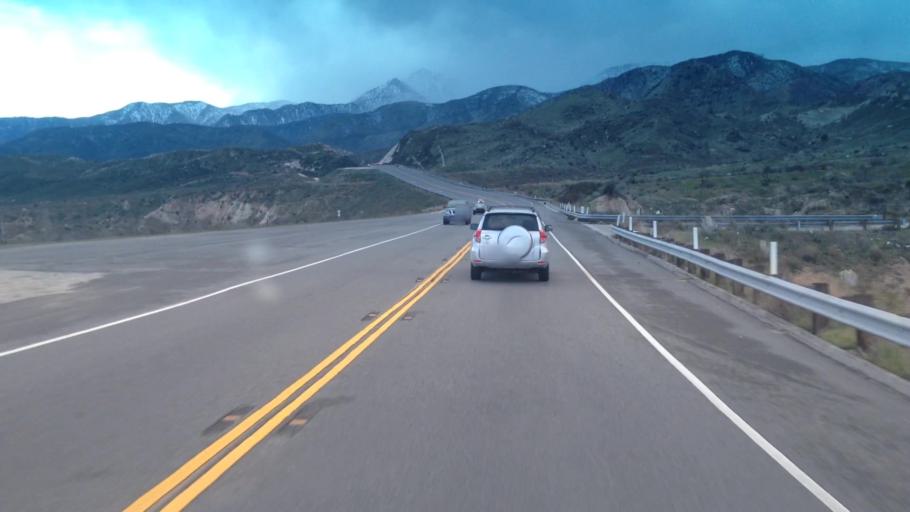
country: US
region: California
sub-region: San Bernardino County
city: Oak Hills
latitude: 34.3210
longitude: -117.4601
